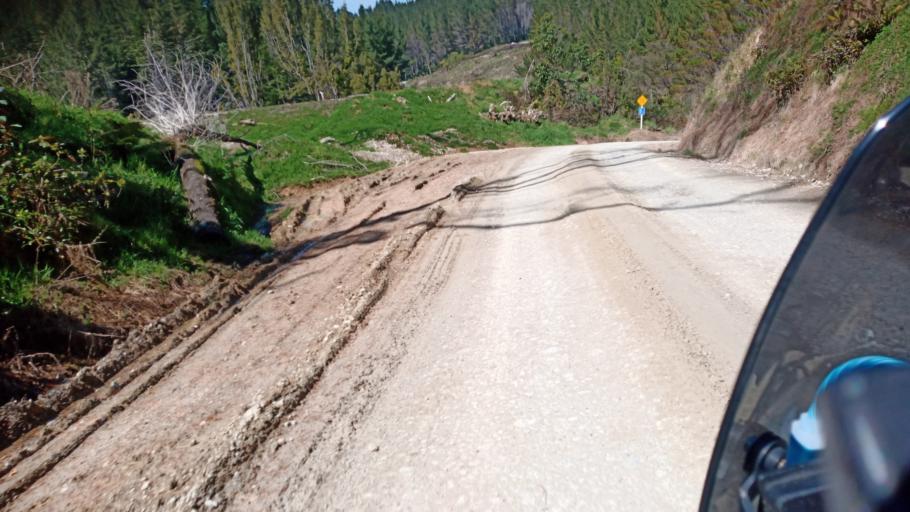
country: NZ
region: Gisborne
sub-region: Gisborne District
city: Gisborne
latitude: -38.8936
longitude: 177.7997
